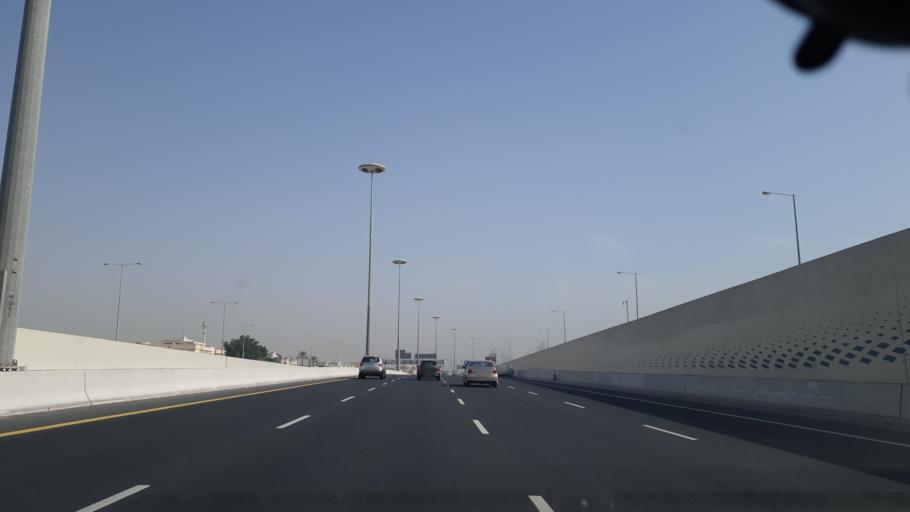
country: QA
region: Baladiyat ad Dawhah
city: Doha
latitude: 25.3558
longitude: 51.5203
